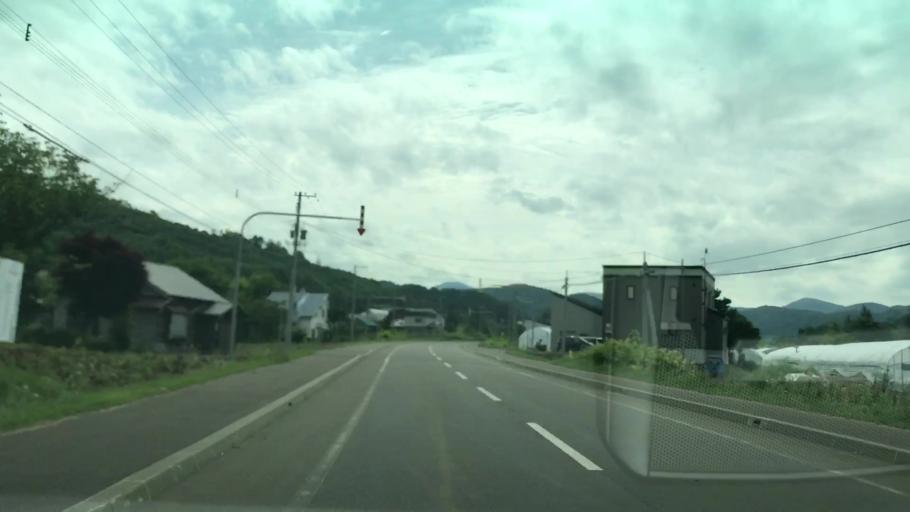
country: JP
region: Hokkaido
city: Yoichi
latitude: 43.1848
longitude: 140.8431
